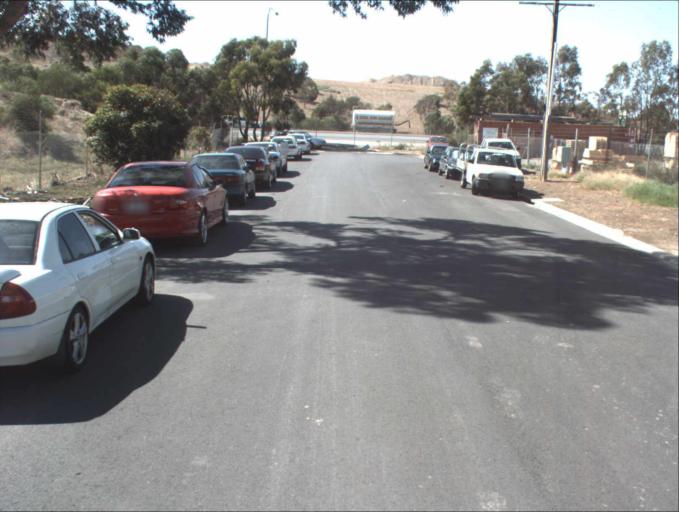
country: AU
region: South Australia
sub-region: Charles Sturt
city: Woodville North
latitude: -34.8340
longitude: 138.5589
